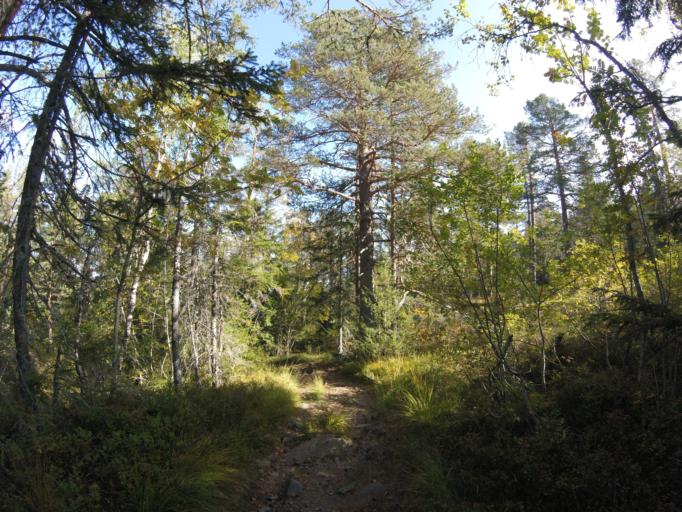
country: NO
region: Buskerud
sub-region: Kongsberg
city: Kongsberg
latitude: 59.6648
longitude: 9.5952
